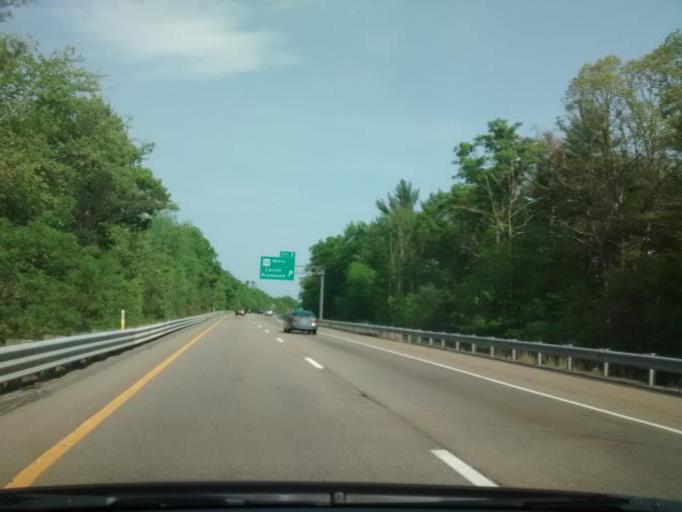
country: US
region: Massachusetts
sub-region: Plymouth County
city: West Wareham
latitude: 41.8086
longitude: -70.7762
